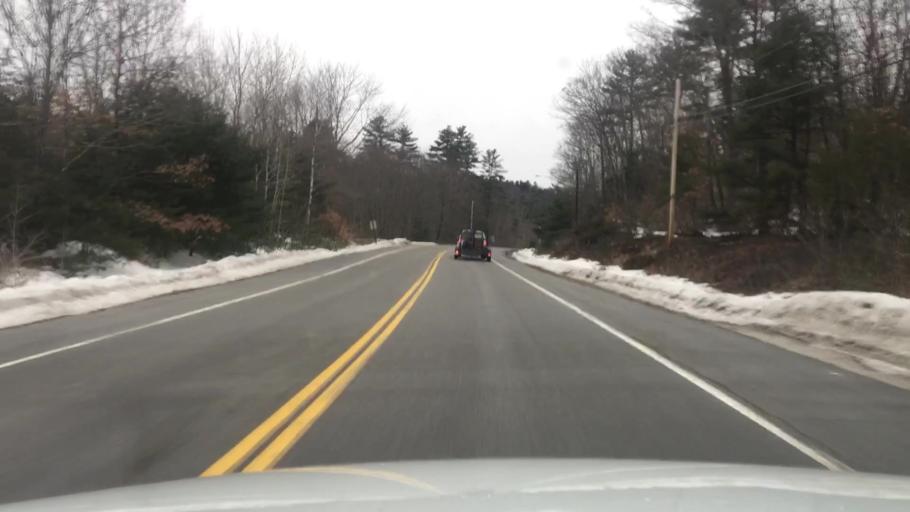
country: US
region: Maine
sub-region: York County
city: Limerick
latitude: 43.7339
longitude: -70.8161
